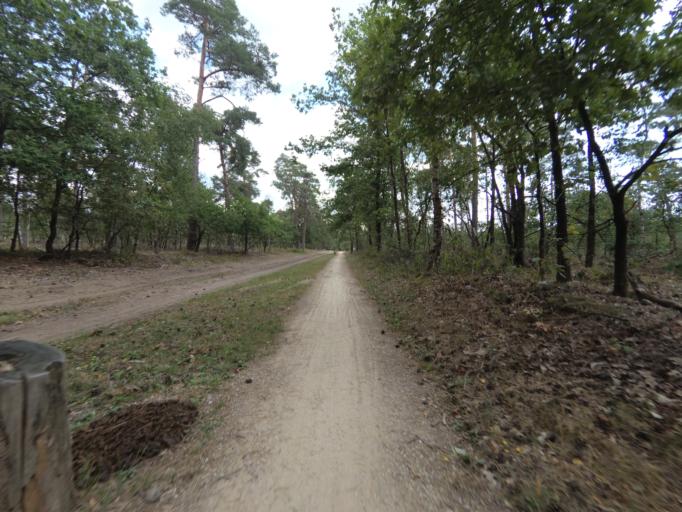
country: NL
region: Overijssel
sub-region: Gemeente Haaksbergen
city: Haaksbergen
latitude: 52.1267
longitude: 6.7209
